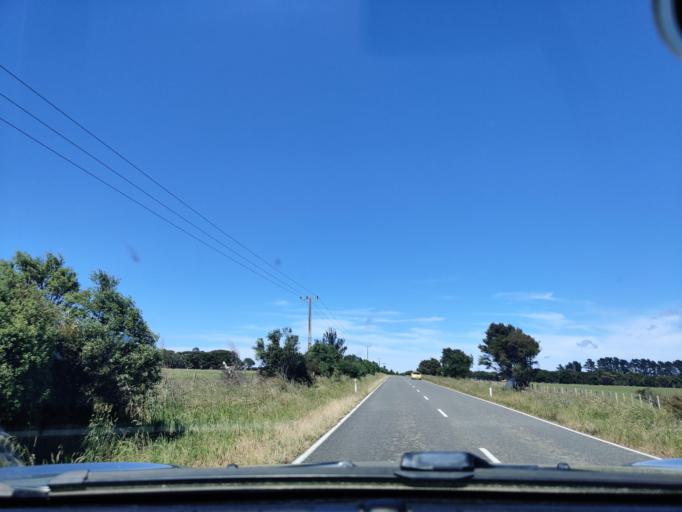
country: NZ
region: Wellington
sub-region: Upper Hutt City
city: Upper Hutt
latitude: -41.3245
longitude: 175.2459
